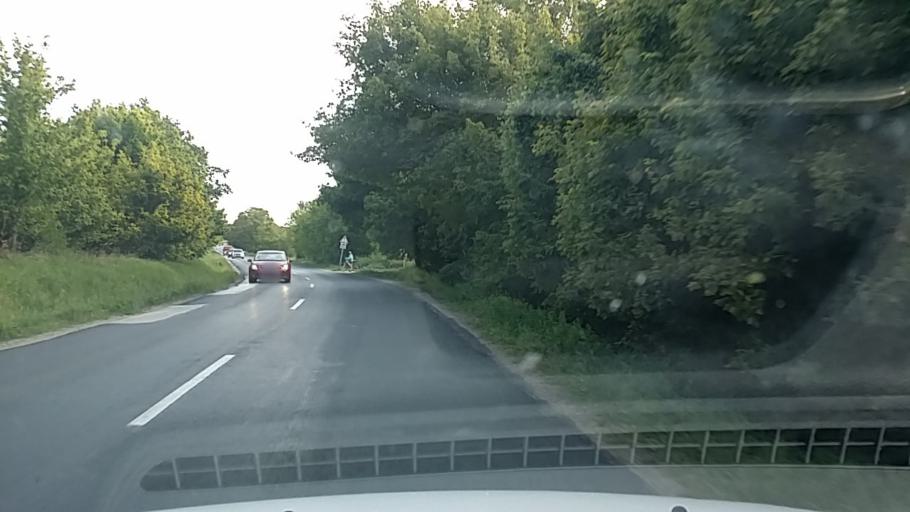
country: HU
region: Gyor-Moson-Sopron
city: Sopron
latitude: 47.7042
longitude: 16.6056
